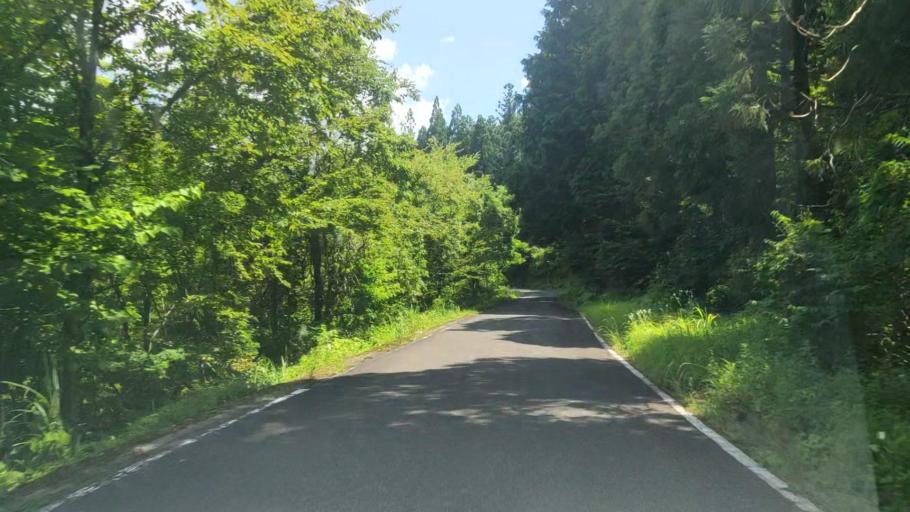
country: JP
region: Fukui
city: Ono
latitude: 35.7553
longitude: 136.5737
